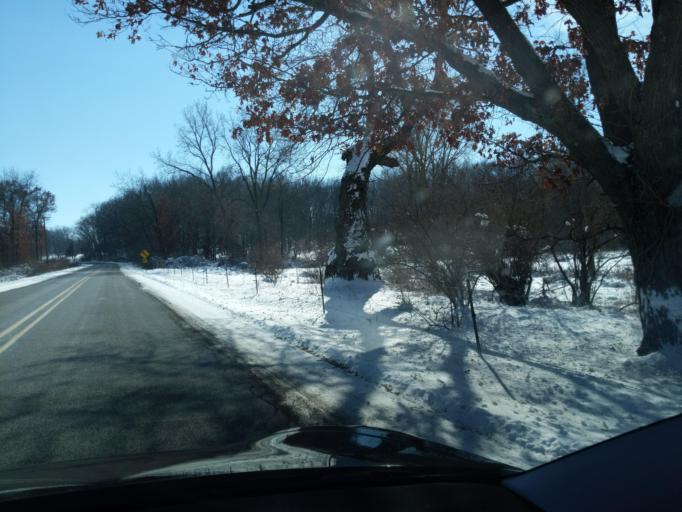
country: US
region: Michigan
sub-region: Ingham County
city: Stockbridge
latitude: 42.4975
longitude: -84.0887
